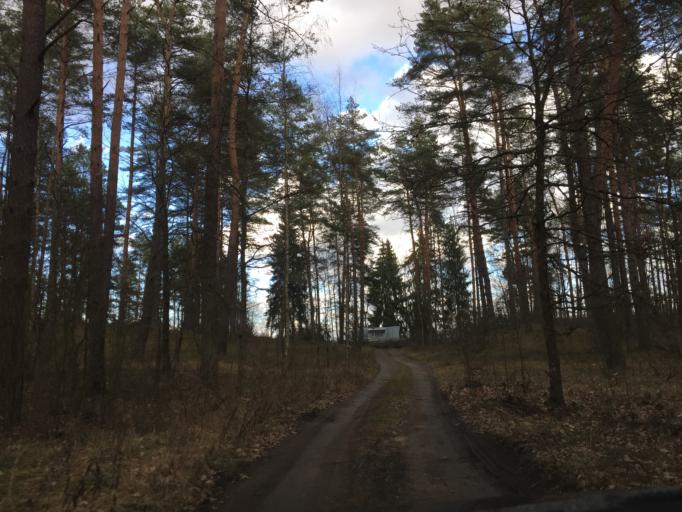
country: LV
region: Adazi
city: Adazi
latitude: 57.0582
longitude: 24.3341
